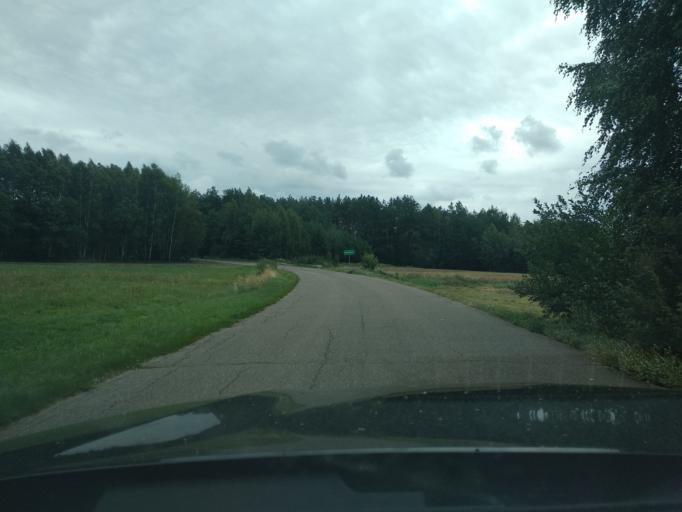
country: PL
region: Masovian Voivodeship
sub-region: Powiat pultuski
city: Obryte
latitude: 52.7443
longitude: 21.2145
